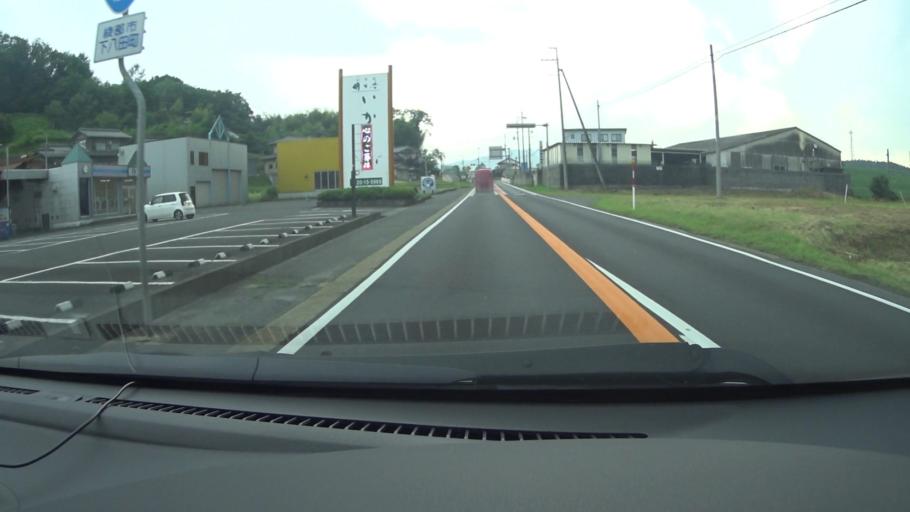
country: JP
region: Kyoto
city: Ayabe
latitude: 35.3104
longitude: 135.2782
